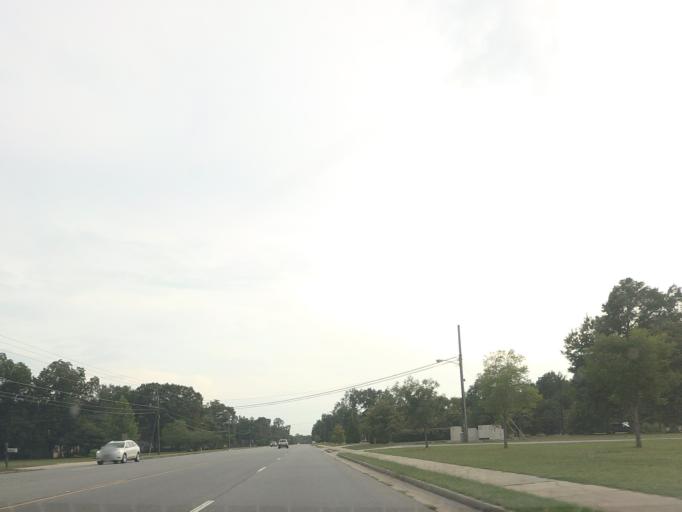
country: US
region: Georgia
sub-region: Houston County
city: Centerville
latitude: 32.7366
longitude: -83.6777
